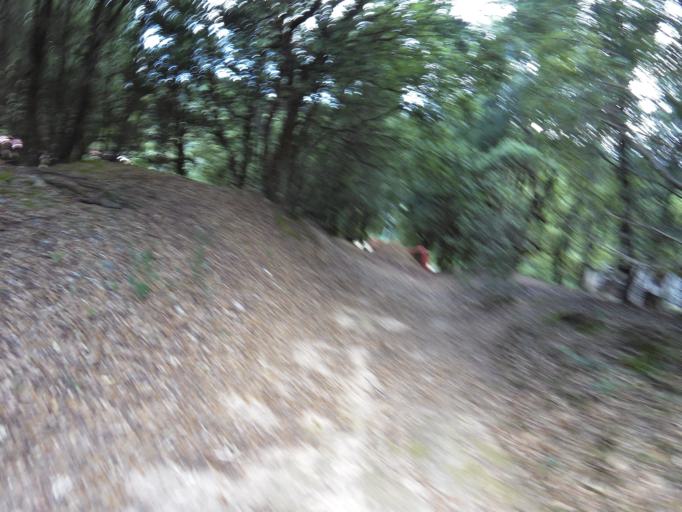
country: IT
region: Calabria
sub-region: Provincia di Reggio Calabria
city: Pazzano
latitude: 38.4789
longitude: 16.4019
